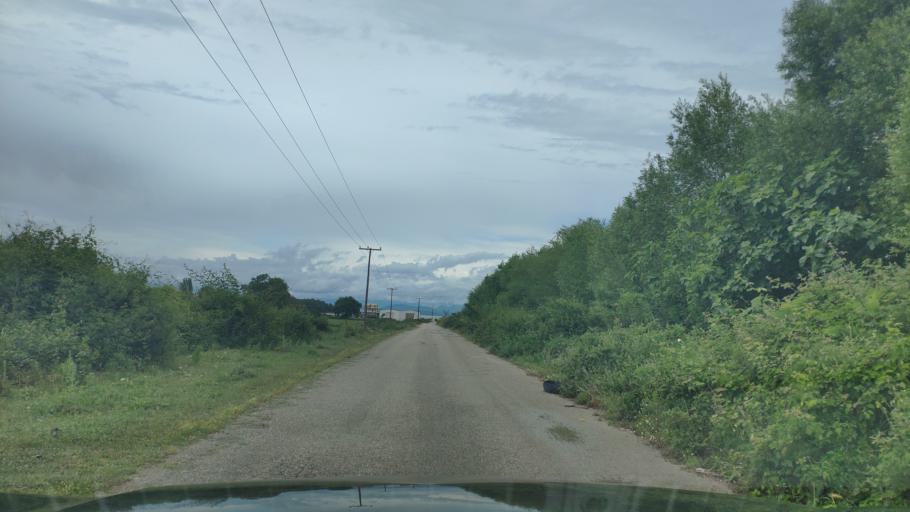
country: GR
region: West Greece
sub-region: Nomos Aitolias kai Akarnanias
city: Vonitsa
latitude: 38.9153
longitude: 20.9076
